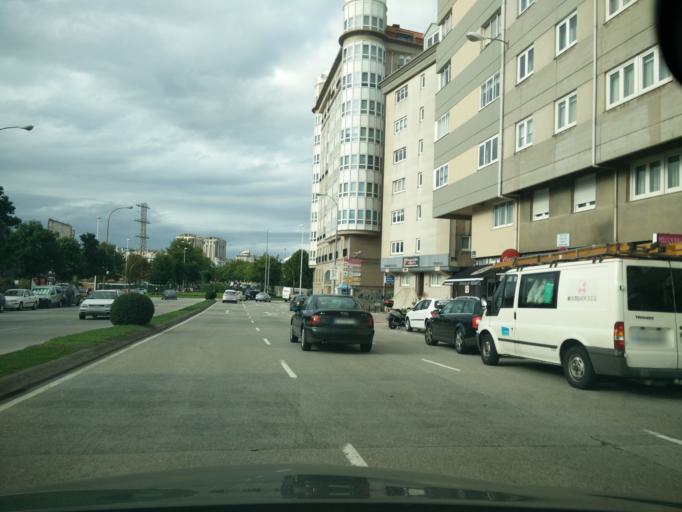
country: ES
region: Galicia
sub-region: Provincia da Coruna
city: A Coruna
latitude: 43.3672
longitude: -8.4245
